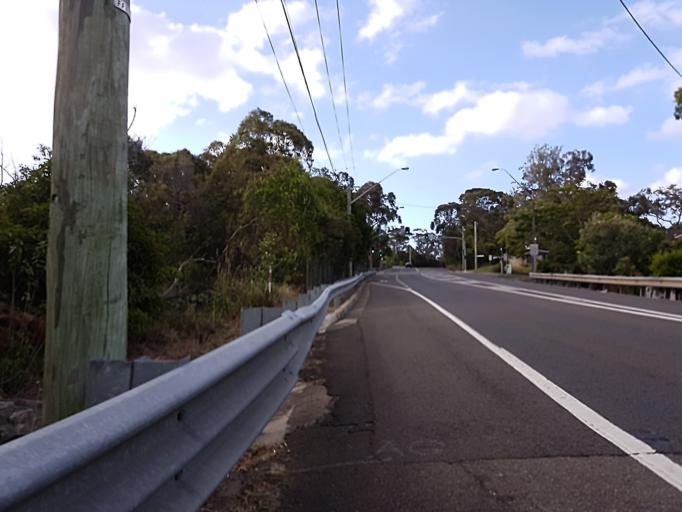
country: AU
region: New South Wales
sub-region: Warringah
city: Killarney Heights
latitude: -33.7835
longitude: 151.2385
